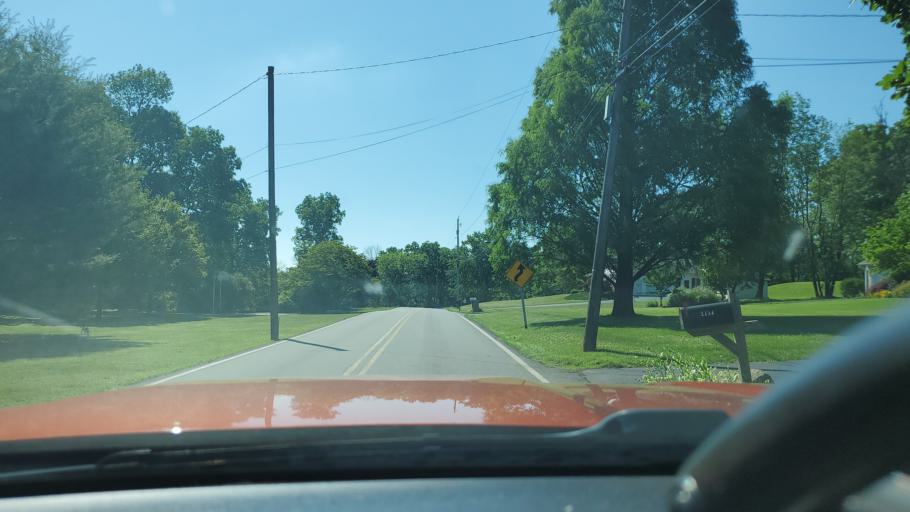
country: US
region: Pennsylvania
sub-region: Montgomery County
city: Red Hill
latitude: 40.3542
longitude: -75.5275
